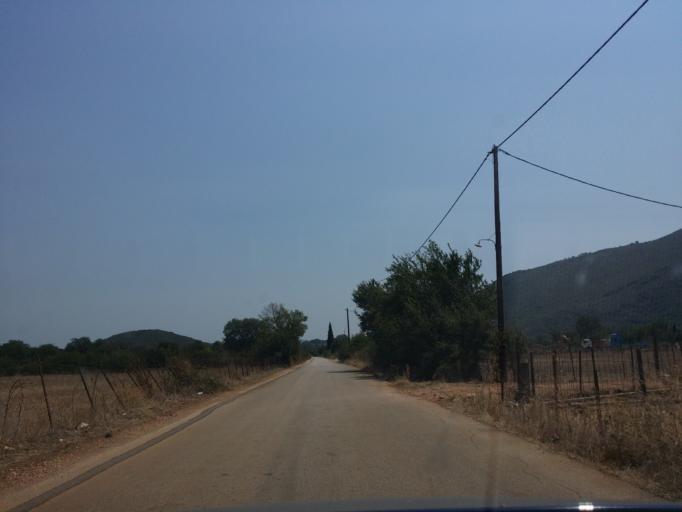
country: GR
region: West Greece
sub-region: Nomos Aitolias kai Akarnanias
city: Archontochorion
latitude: 38.7030
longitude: 21.0889
